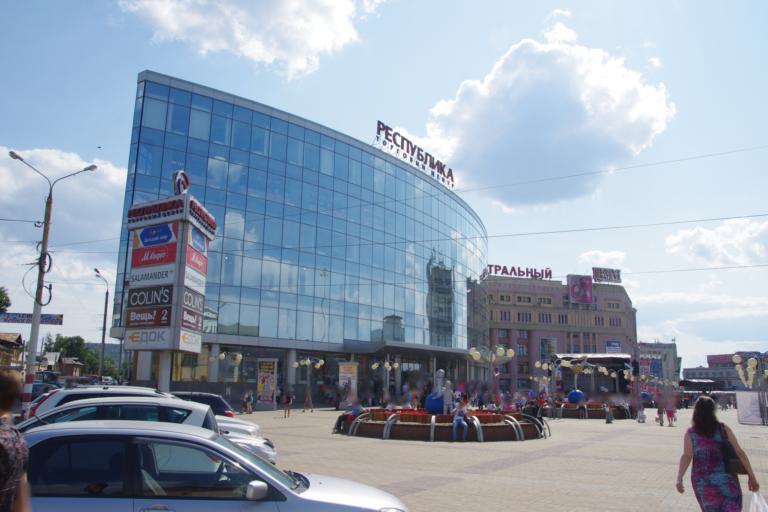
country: RU
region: Nizjnij Novgorod
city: Nizhniy Novgorod
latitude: 56.3213
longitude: 43.9482
